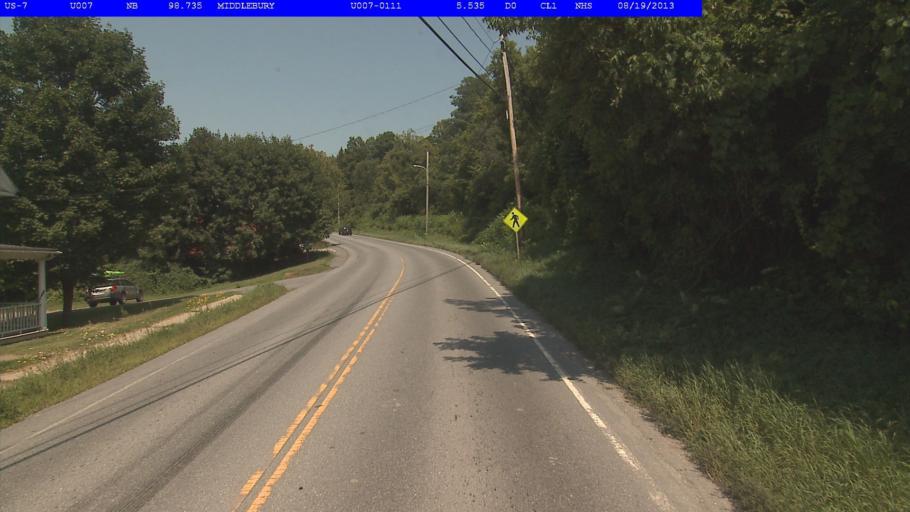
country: US
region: Vermont
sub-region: Addison County
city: Middlebury (village)
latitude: 44.0205
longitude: -73.1654
